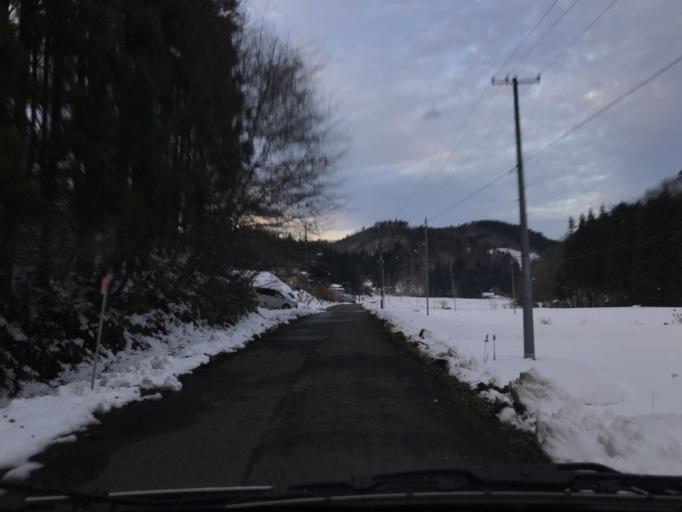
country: JP
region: Iwate
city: Mizusawa
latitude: 39.0429
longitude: 141.0113
